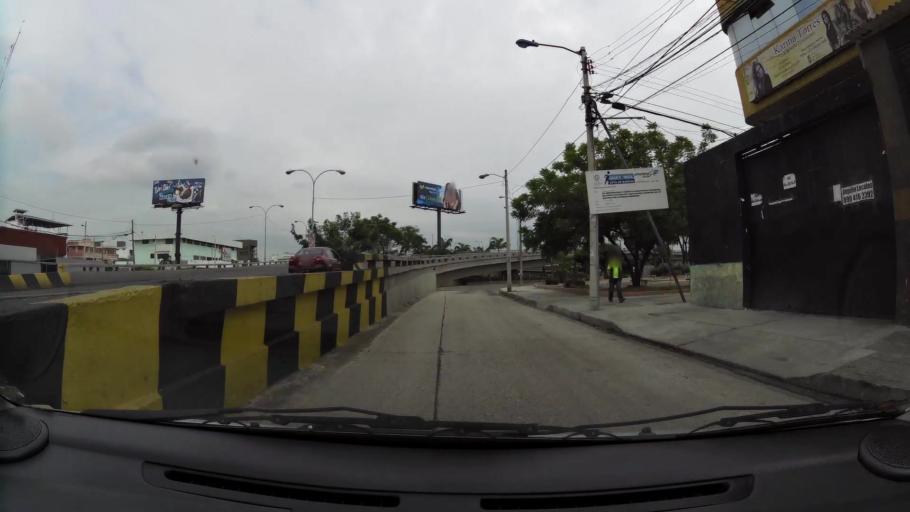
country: EC
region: Guayas
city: Eloy Alfaro
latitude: -2.1527
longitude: -79.8944
